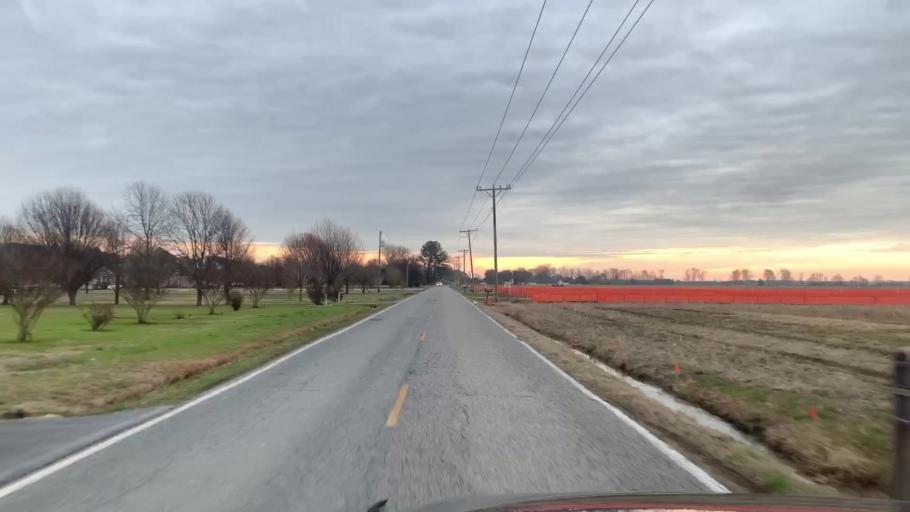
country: US
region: North Carolina
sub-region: Currituck County
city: Moyock
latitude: 36.6295
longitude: -76.1729
